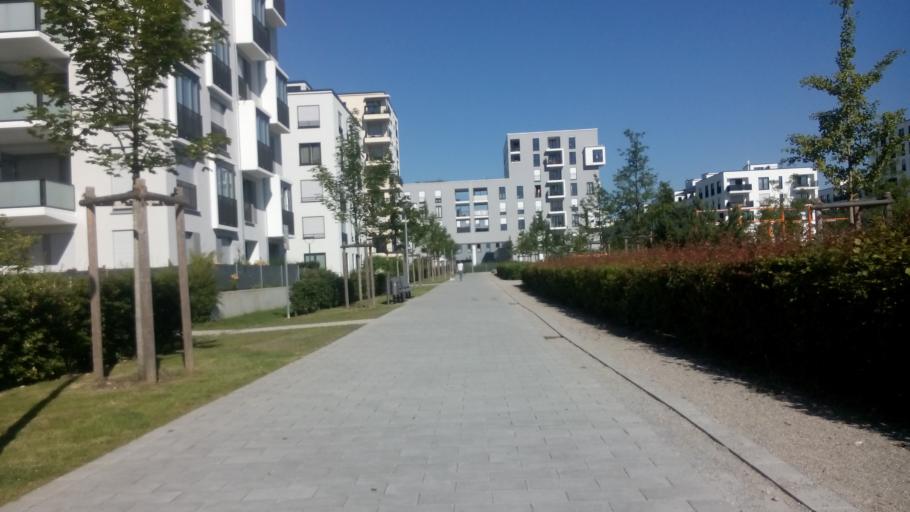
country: DE
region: Bavaria
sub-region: Upper Bavaria
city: Munich
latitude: 48.1095
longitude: 11.5829
